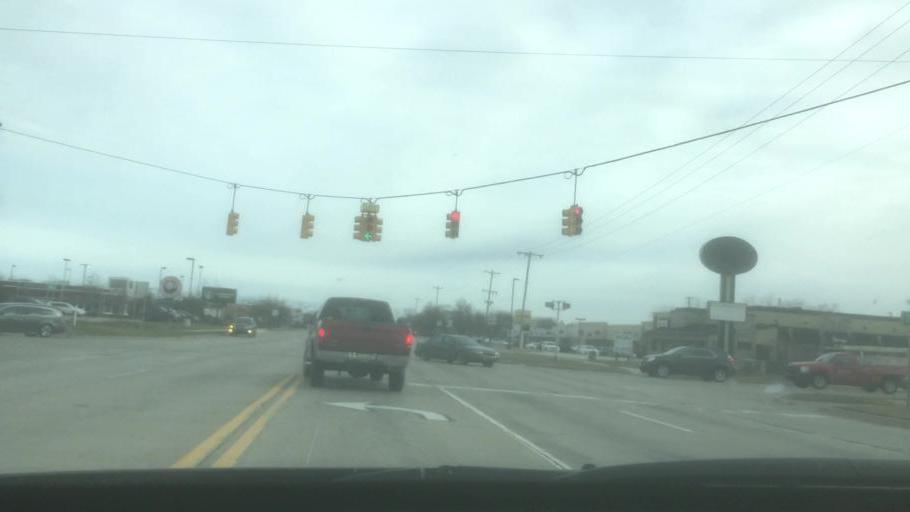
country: US
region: Michigan
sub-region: Bay County
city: Bay City
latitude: 43.6240
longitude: -83.8946
